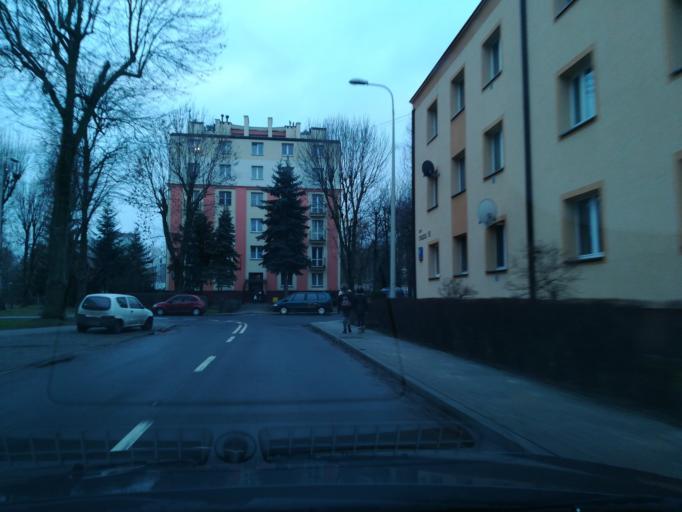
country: PL
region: Subcarpathian Voivodeship
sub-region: Rzeszow
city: Rzeszow
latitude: 50.0270
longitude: 21.9939
